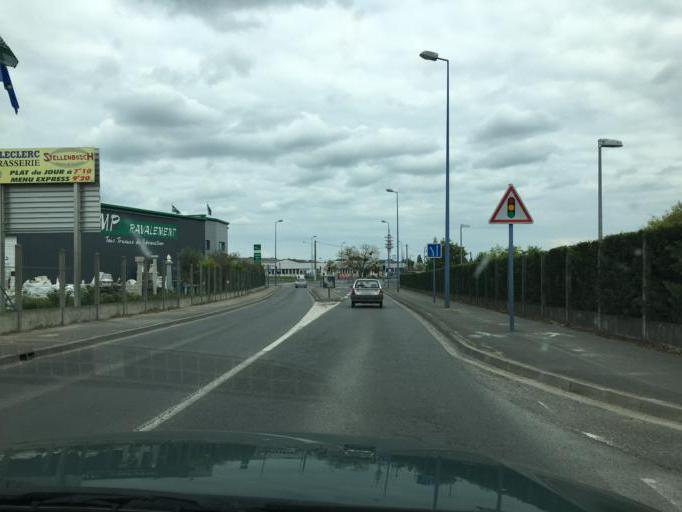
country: FR
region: Centre
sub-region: Departement du Loiret
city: Fleury-les-Aubrais
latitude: 47.9454
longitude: 1.9119
